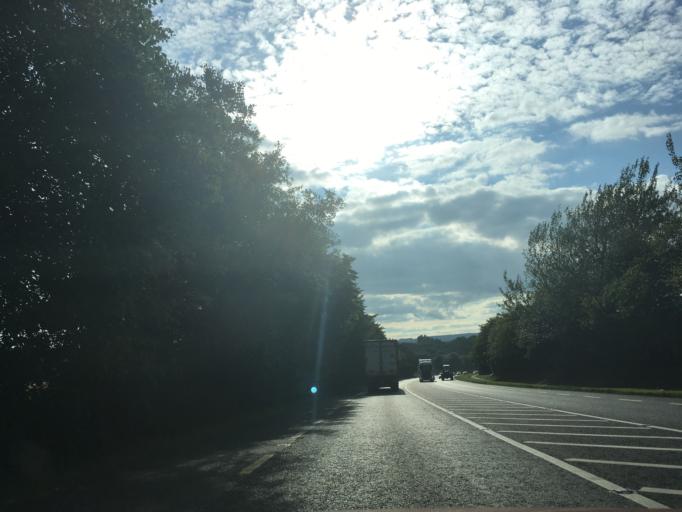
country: IE
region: Leinster
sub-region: Loch Garman
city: New Ross
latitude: 52.3819
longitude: -6.9380
